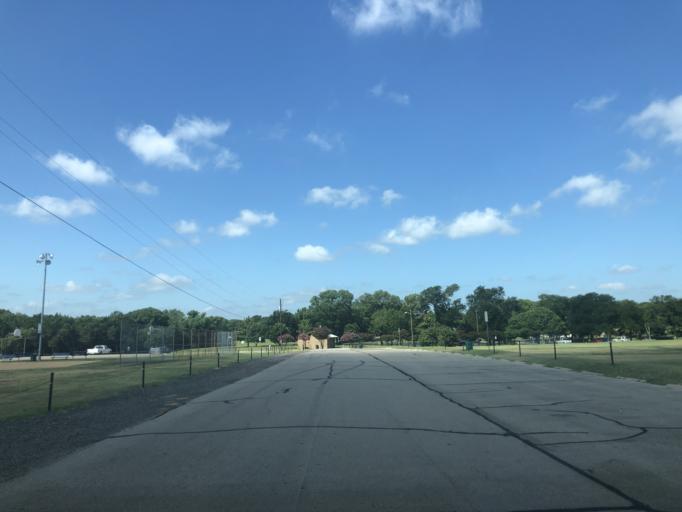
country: US
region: Texas
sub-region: Dallas County
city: Duncanville
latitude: 32.6564
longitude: -96.9182
